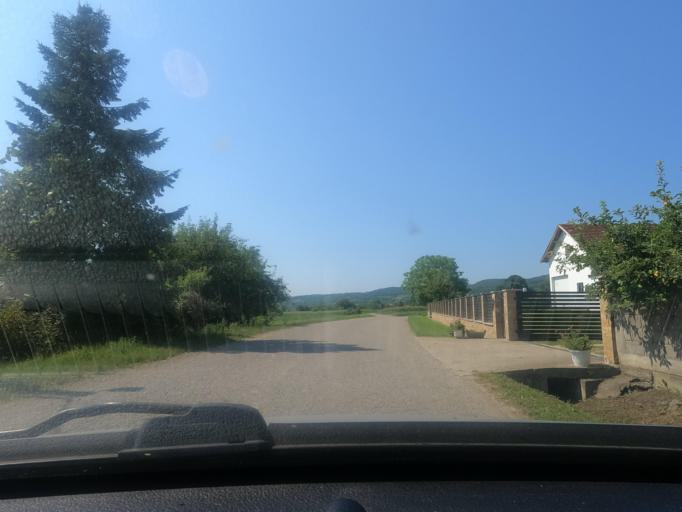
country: RS
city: Jarebice
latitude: 44.5365
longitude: 19.3727
